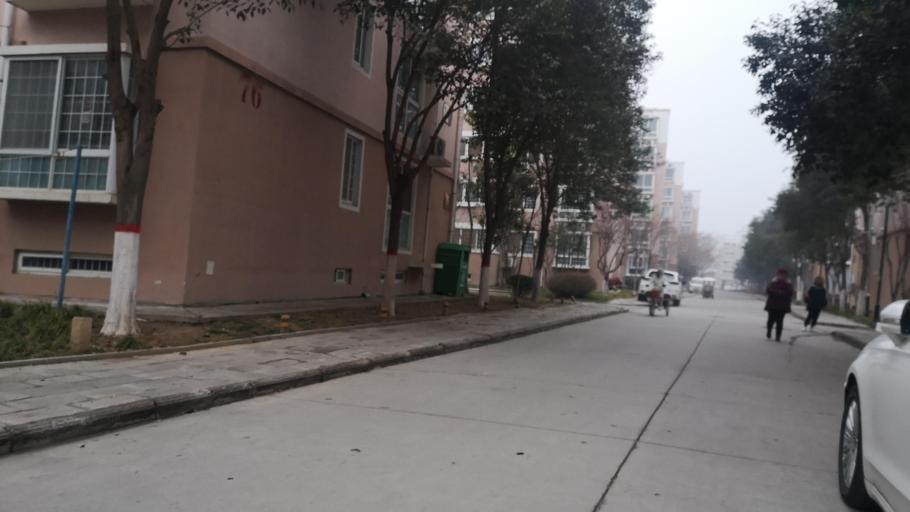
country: CN
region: Henan Sheng
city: Zhongyuanlu
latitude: 35.7852
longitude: 115.0882
